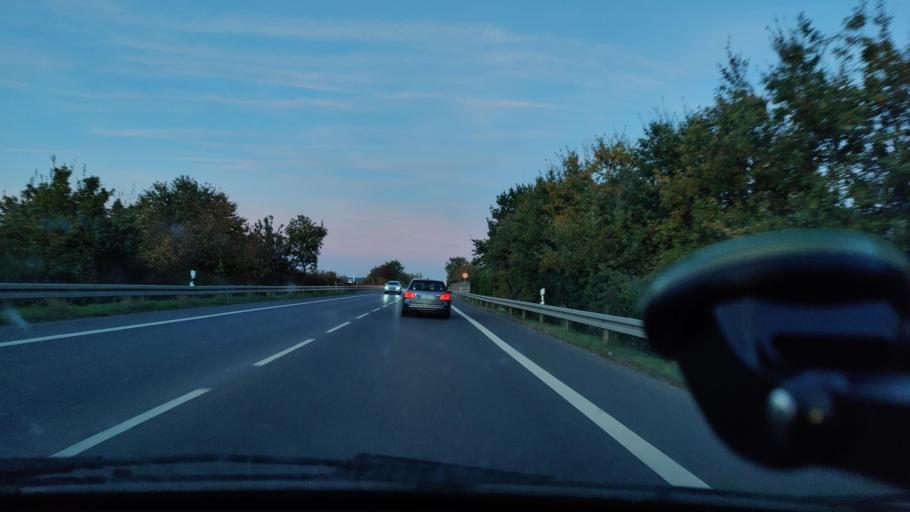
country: DE
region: North Rhine-Westphalia
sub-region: Regierungsbezirk Koln
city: Heinsberg
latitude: 51.0605
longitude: 6.1147
